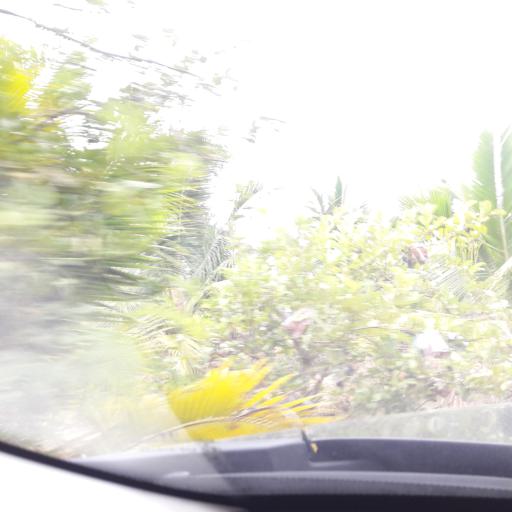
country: TH
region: Ratchaburi
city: Damnoen Saduak
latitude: 13.5767
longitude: 99.9486
